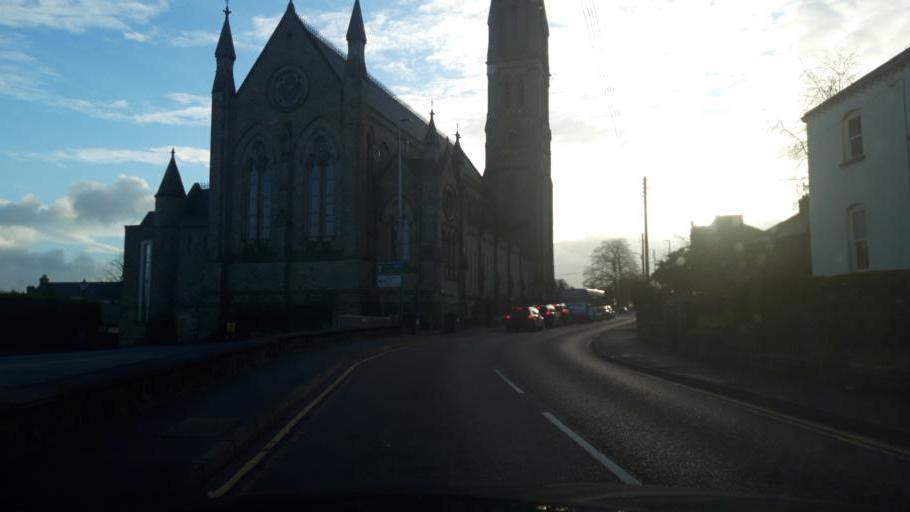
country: GB
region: Northern Ireland
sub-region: Dungannon District
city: Dungannon
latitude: 54.5060
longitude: -6.7637
